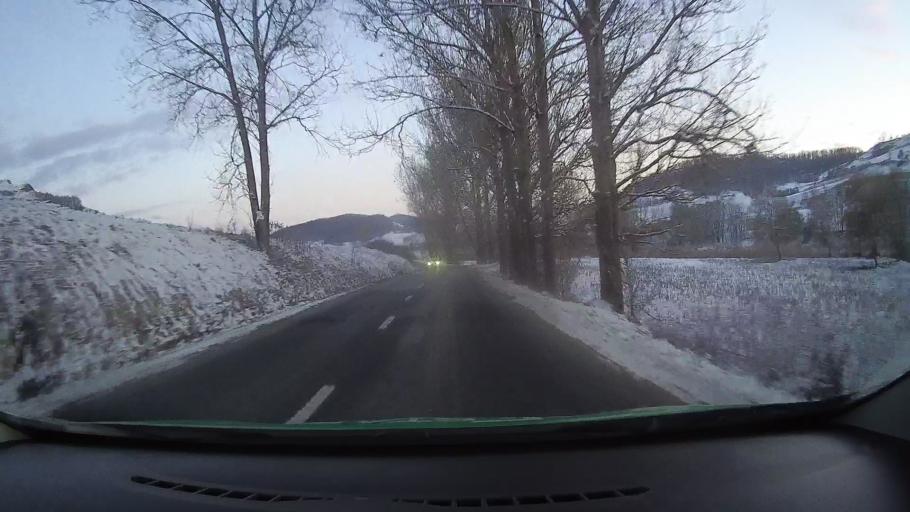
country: RO
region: Sibiu
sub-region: Comuna Alma
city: Alma
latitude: 46.1968
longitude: 24.4706
